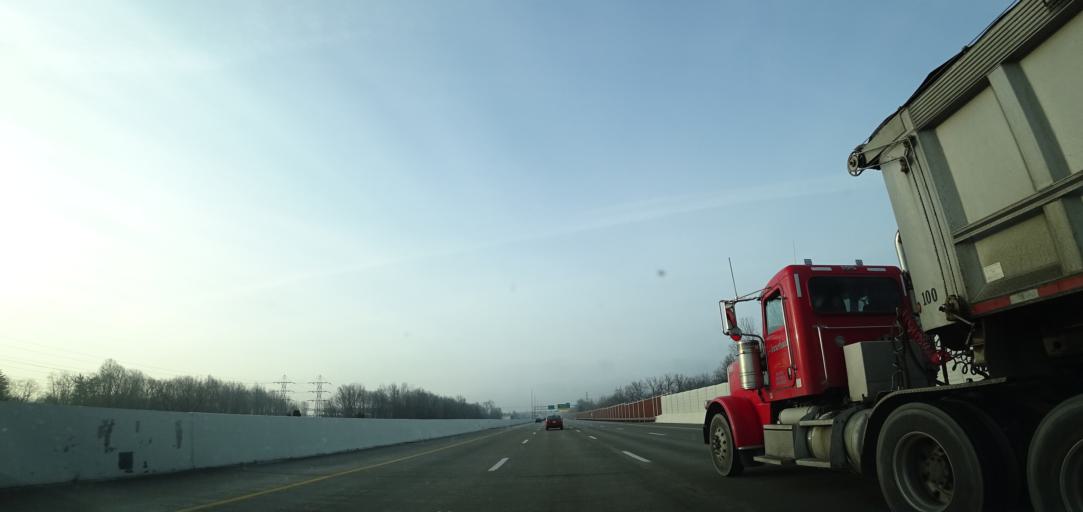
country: US
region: Ohio
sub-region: Cuyahoga County
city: Independence
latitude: 41.3698
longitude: -81.6519
